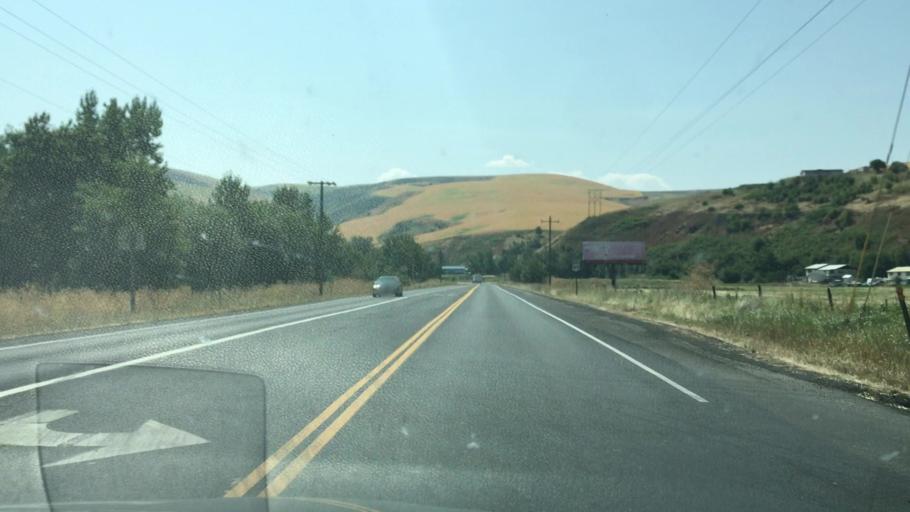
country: US
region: Idaho
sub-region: Nez Perce County
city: Lapwai
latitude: 46.3655
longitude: -116.7949
